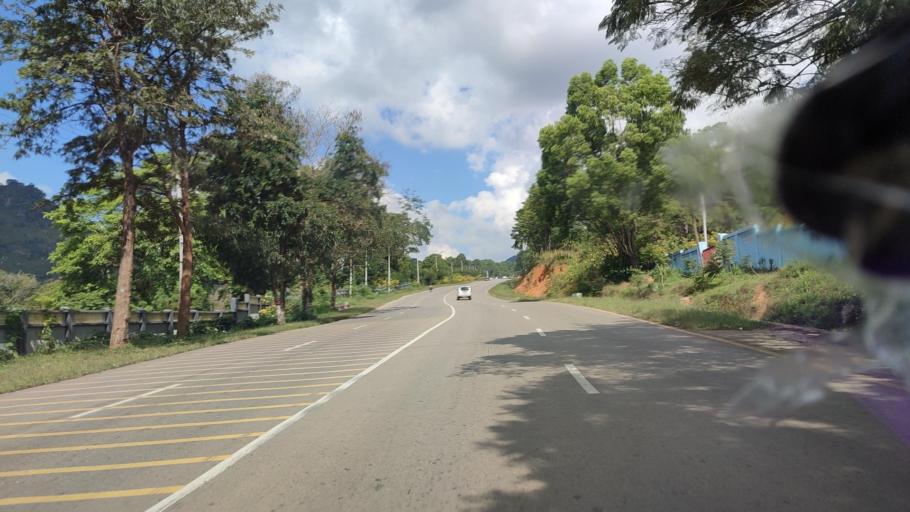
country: MM
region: Shan
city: Taunggyi
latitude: 20.6445
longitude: 96.5916
